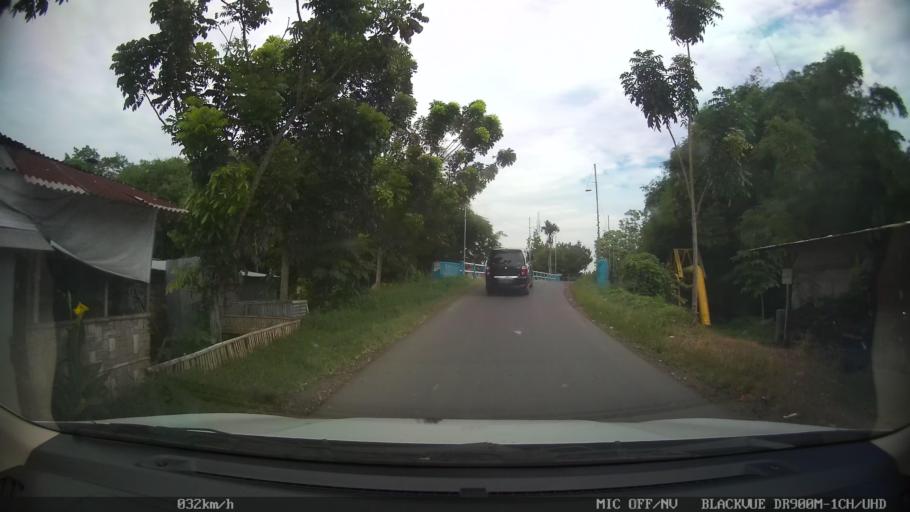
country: ID
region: North Sumatra
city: Sunggal
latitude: 3.6621
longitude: 98.5923
